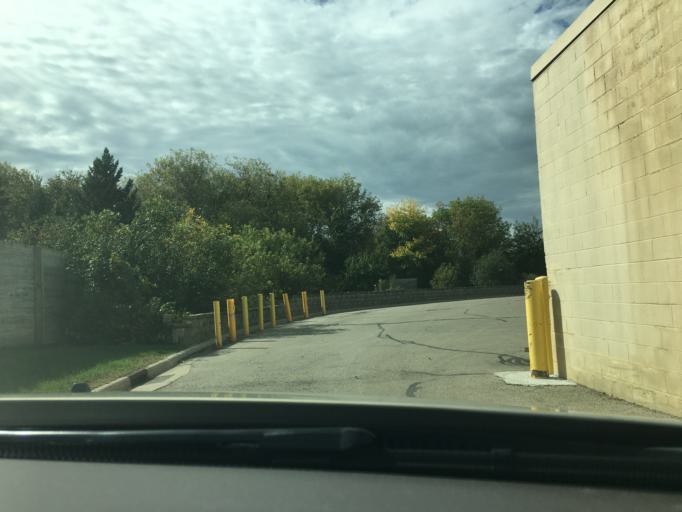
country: US
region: Minnesota
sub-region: Olmsted County
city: Rochester
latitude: 44.0047
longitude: -92.4704
